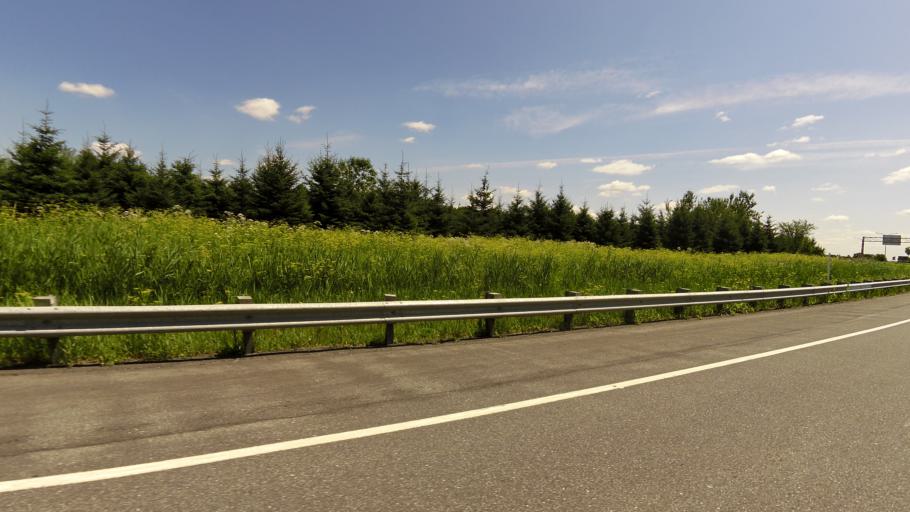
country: CA
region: Quebec
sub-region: Monteregie
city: Carignan
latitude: 45.4041
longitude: -73.3145
